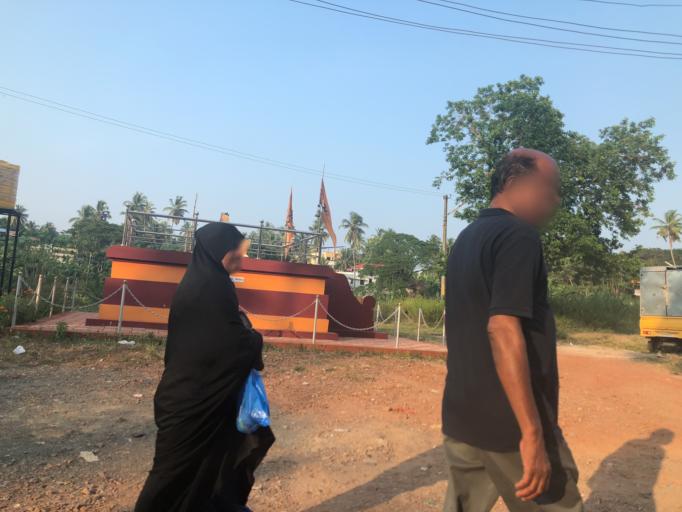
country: IN
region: Karnataka
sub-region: Dakshina Kannada
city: Ullal
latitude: 12.8461
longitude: 74.8501
